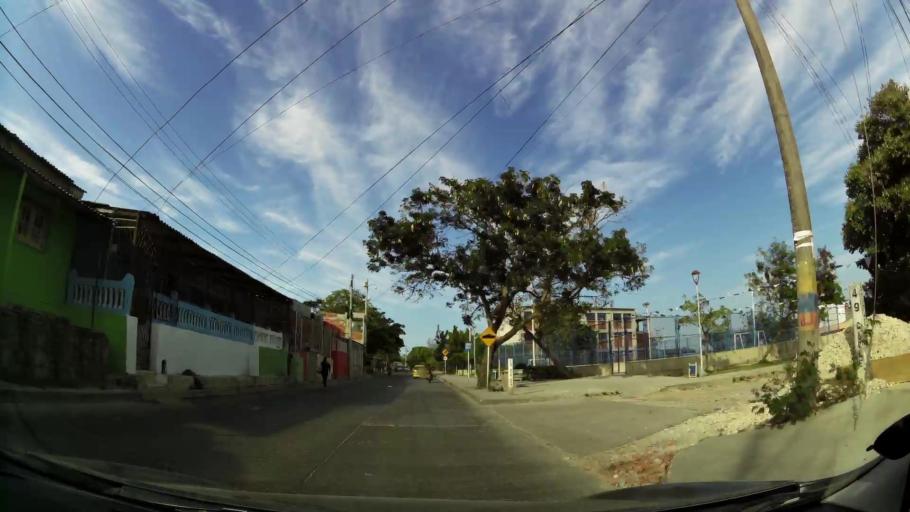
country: CO
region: Atlantico
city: Soledad
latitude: 10.9271
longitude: -74.8111
